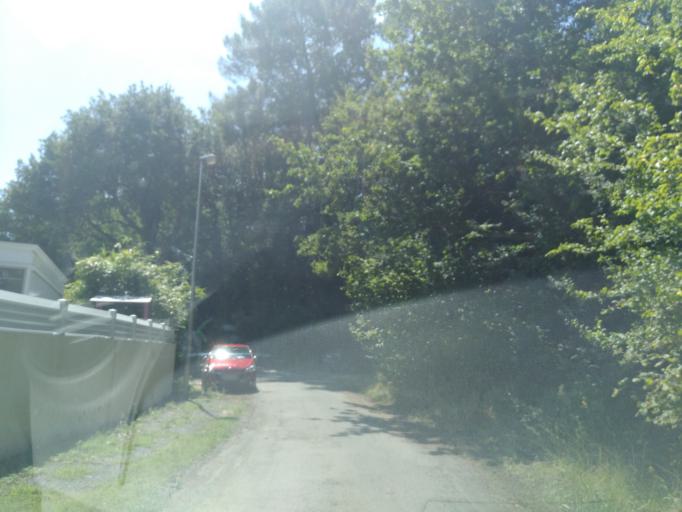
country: FR
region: Poitou-Charentes
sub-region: Departement de la Charente-Maritime
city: Vaux-sur-Mer
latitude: 45.6619
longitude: -1.0746
